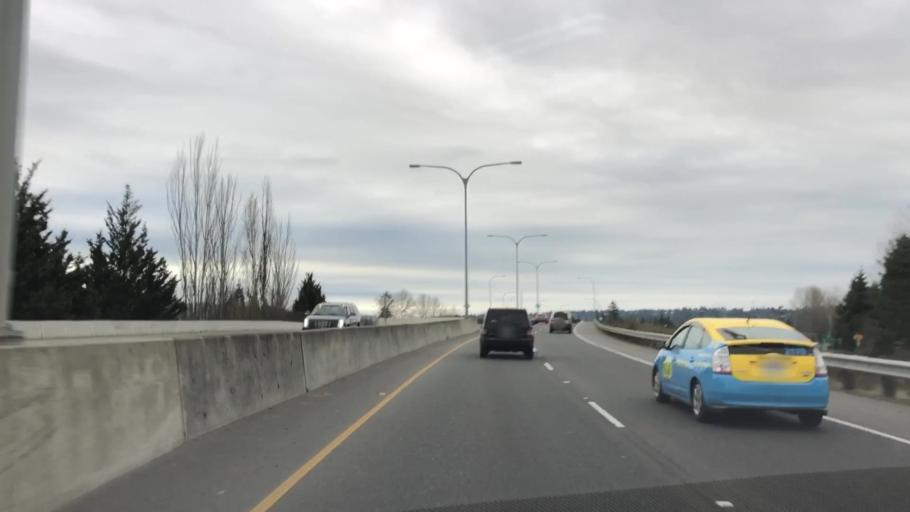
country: US
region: Washington
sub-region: King County
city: Redmond
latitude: 47.6731
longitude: -122.1060
